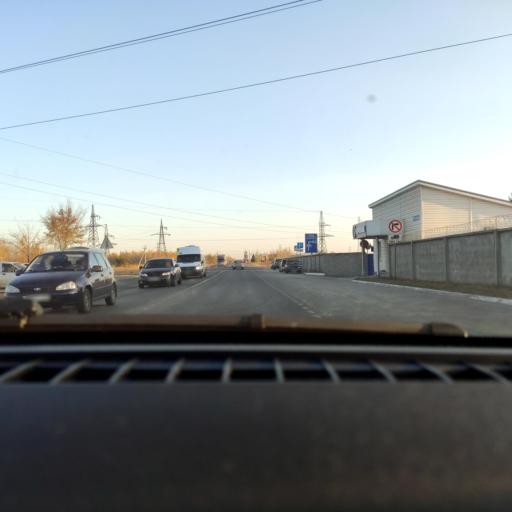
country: RU
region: Voronezj
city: Maslovka
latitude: 51.5894
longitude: 39.2514
